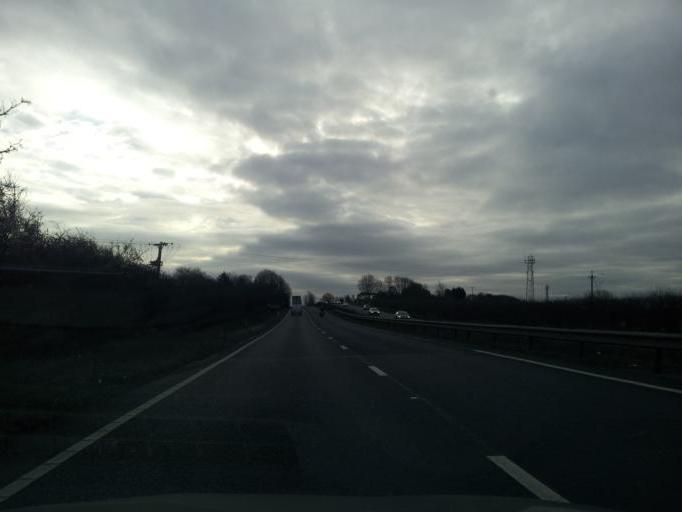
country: GB
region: England
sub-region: Lincolnshire
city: Long Bennington
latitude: 52.9739
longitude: -0.7280
